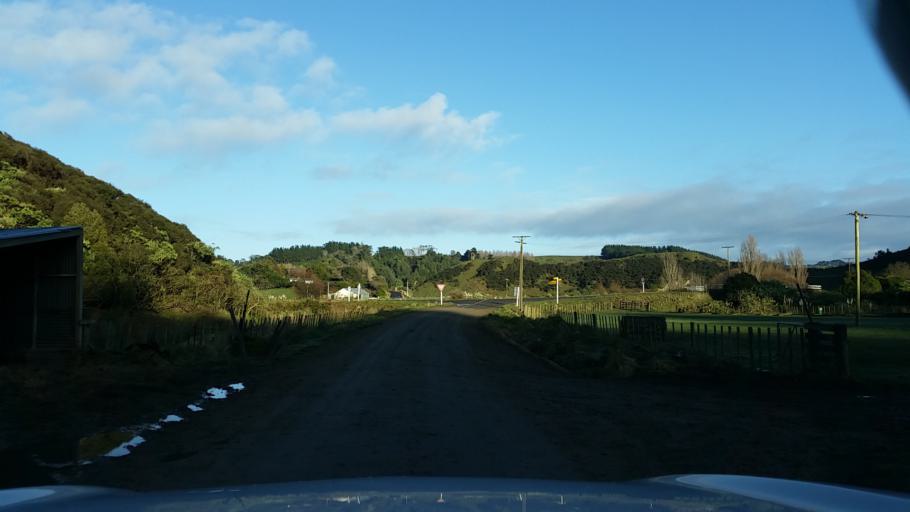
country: NZ
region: Taranaki
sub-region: South Taranaki District
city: Patea
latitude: -39.7599
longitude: 174.7299
